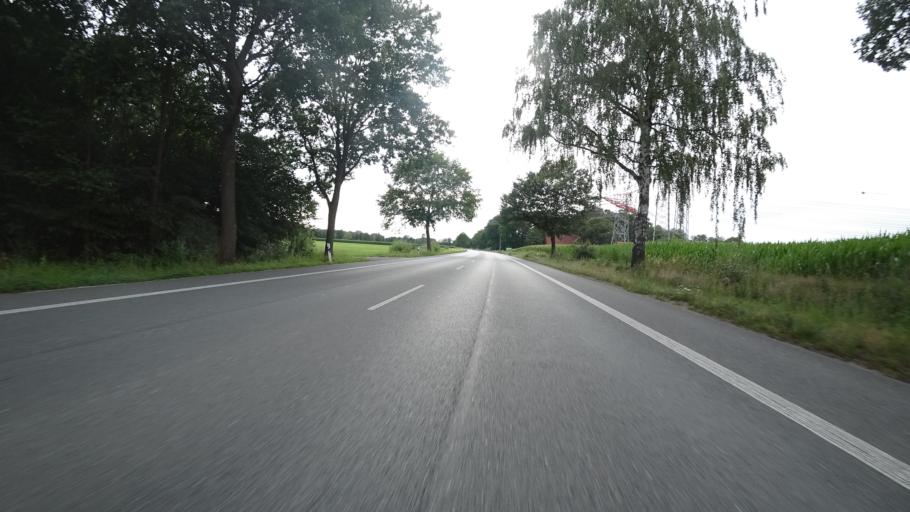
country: DE
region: North Rhine-Westphalia
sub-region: Regierungsbezirk Detmold
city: Guetersloh
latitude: 51.9210
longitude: 8.3508
